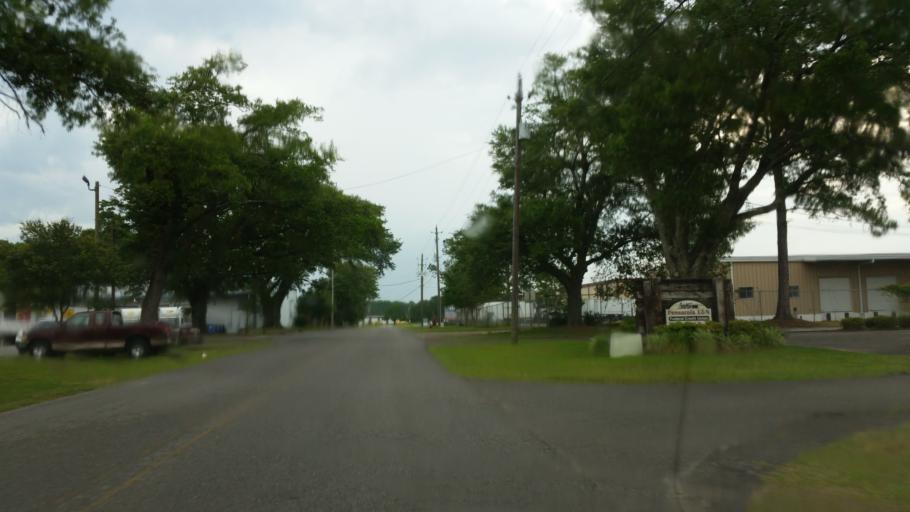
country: US
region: Florida
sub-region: Escambia County
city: Brent
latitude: 30.4658
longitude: -87.2342
